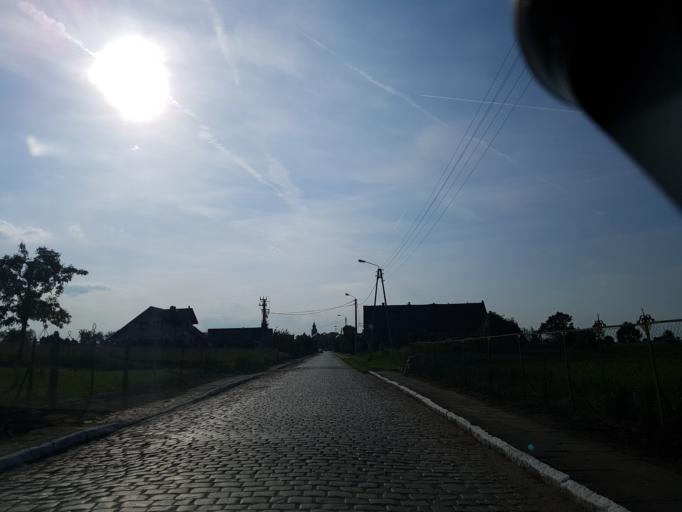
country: PL
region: Lower Silesian Voivodeship
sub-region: Powiat strzelinski
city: Wiazow
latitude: 50.8410
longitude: 17.2178
